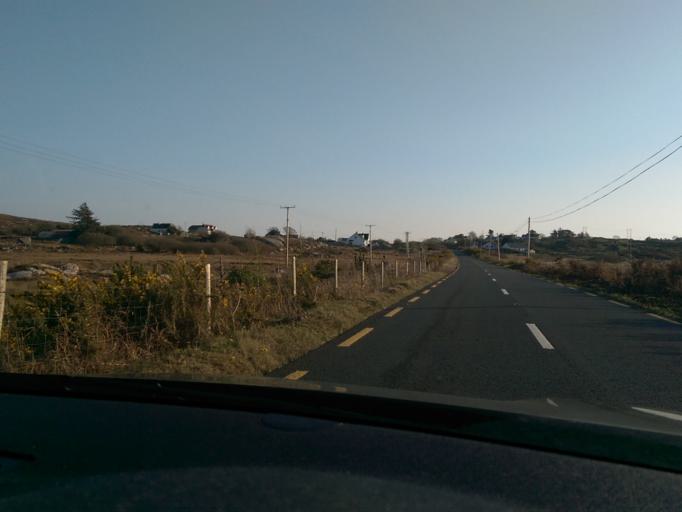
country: IE
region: Connaught
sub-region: County Galway
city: Oughterard
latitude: 53.3458
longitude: -9.5441
